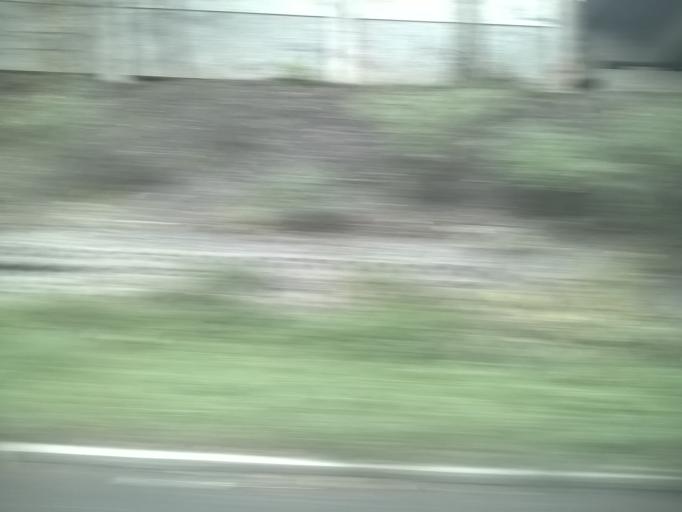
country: FI
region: Pirkanmaa
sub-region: Tampere
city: Tampere
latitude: 61.5063
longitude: 23.7898
